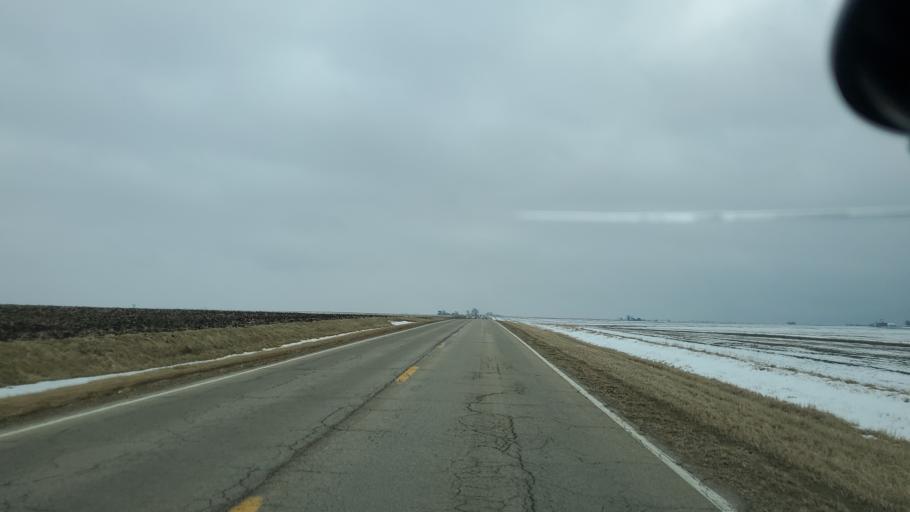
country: US
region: Illinois
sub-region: Marshall County
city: Wenona
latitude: 41.1187
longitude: -89.1336
